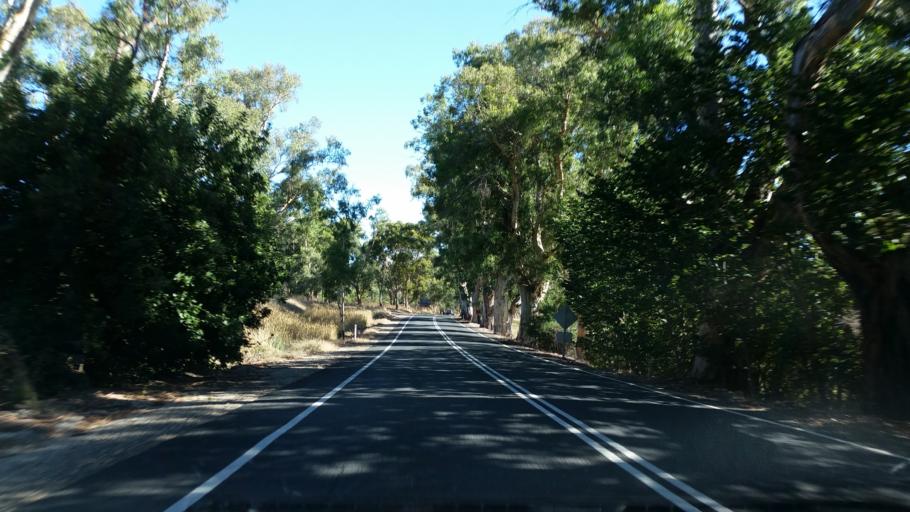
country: AU
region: South Australia
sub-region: Adelaide Hills
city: Birdwood
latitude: -34.8083
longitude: 138.9800
